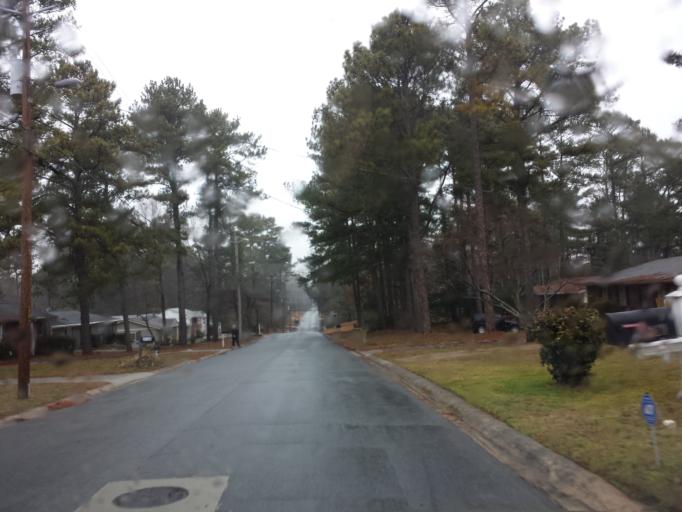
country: US
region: Georgia
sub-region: Cobb County
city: Smyrna
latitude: 33.8859
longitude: -84.4863
